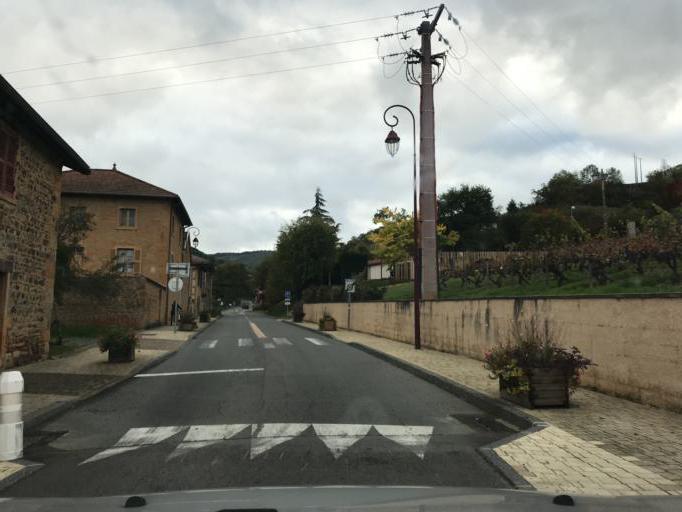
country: FR
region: Rhone-Alpes
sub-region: Departement du Rhone
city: Cogny
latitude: 46.0060
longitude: 4.6016
